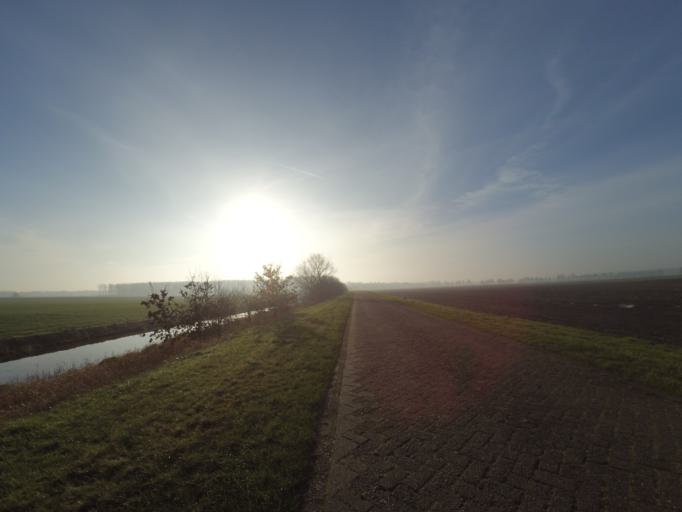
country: NL
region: Drenthe
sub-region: Gemeente Borger-Odoorn
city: Borger
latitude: 52.8977
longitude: 6.7609
